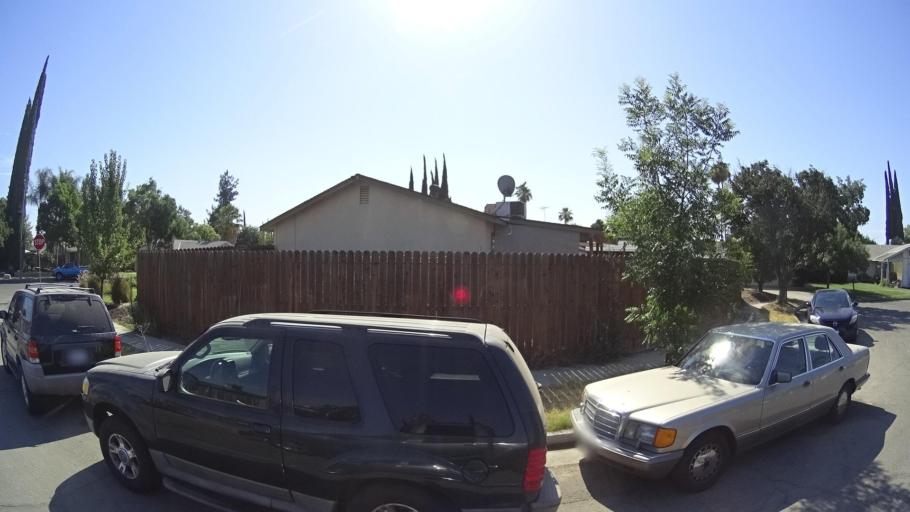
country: US
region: California
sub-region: Fresno County
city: Tarpey Village
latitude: 36.7865
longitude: -119.6853
